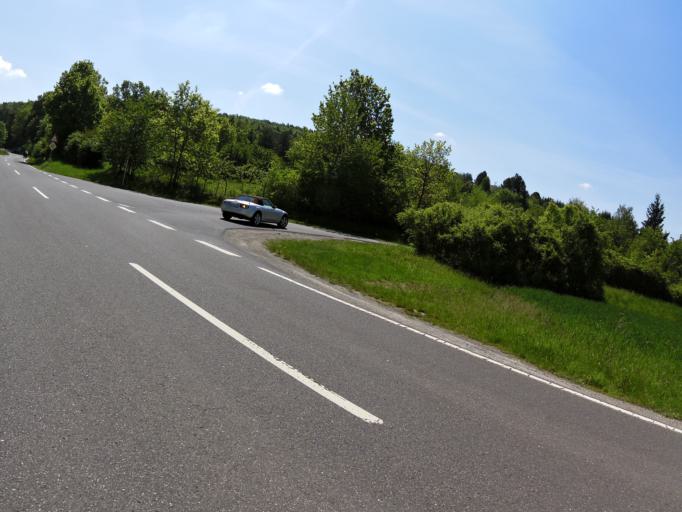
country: DE
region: Bavaria
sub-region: Regierungsbezirk Unterfranken
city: Eibelstadt
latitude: 49.7370
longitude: 10.0019
